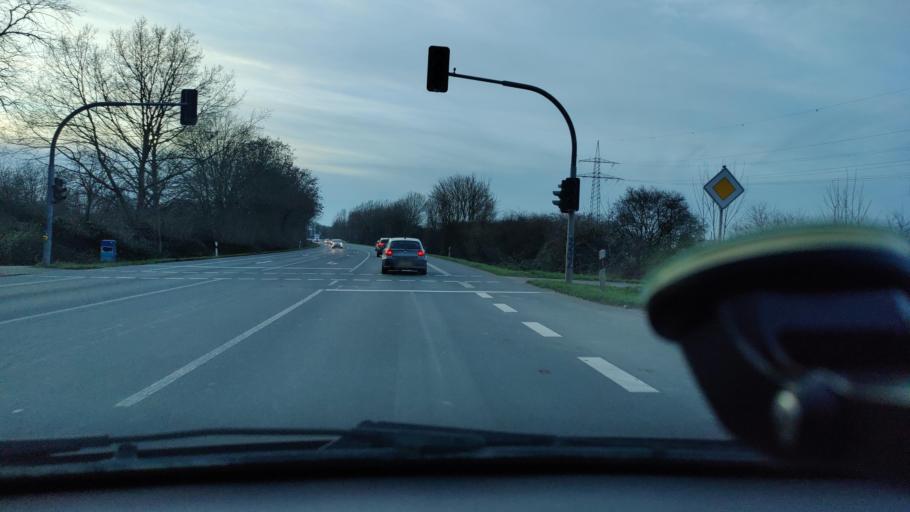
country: DE
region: North Rhine-Westphalia
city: Rheinberg
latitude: 51.5526
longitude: 6.6001
